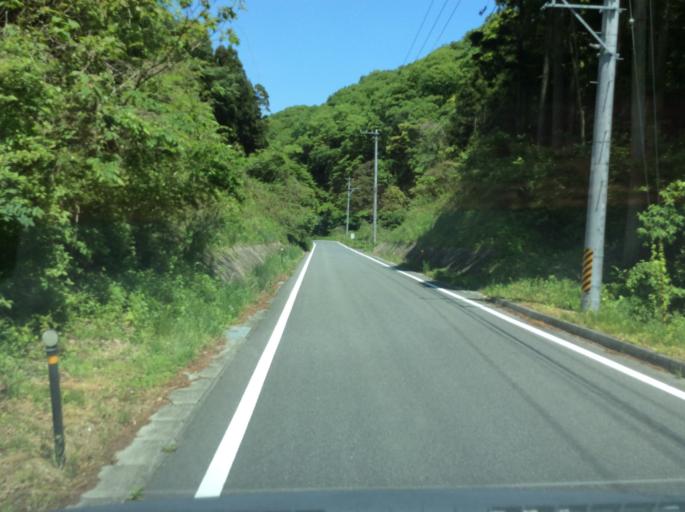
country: JP
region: Fukushima
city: Iwaki
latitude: 37.0056
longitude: 140.9368
